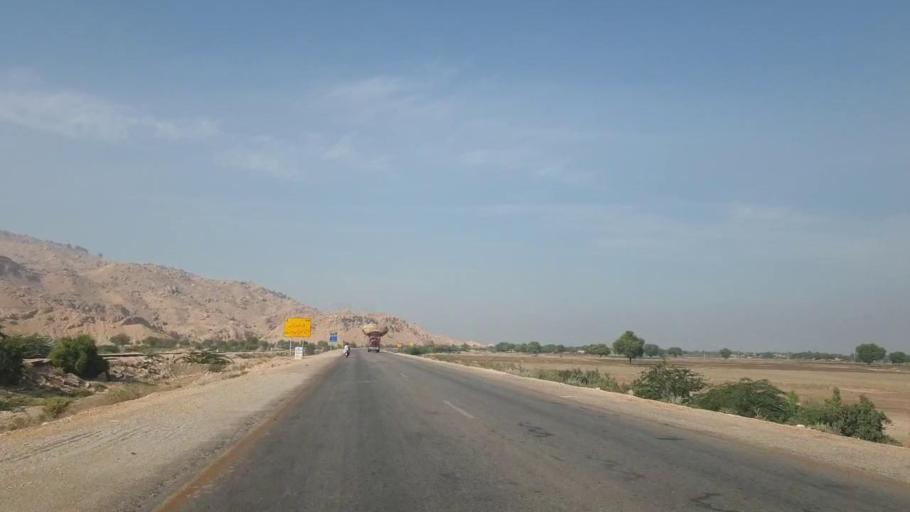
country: PK
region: Sindh
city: Sehwan
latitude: 26.2838
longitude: 67.8954
